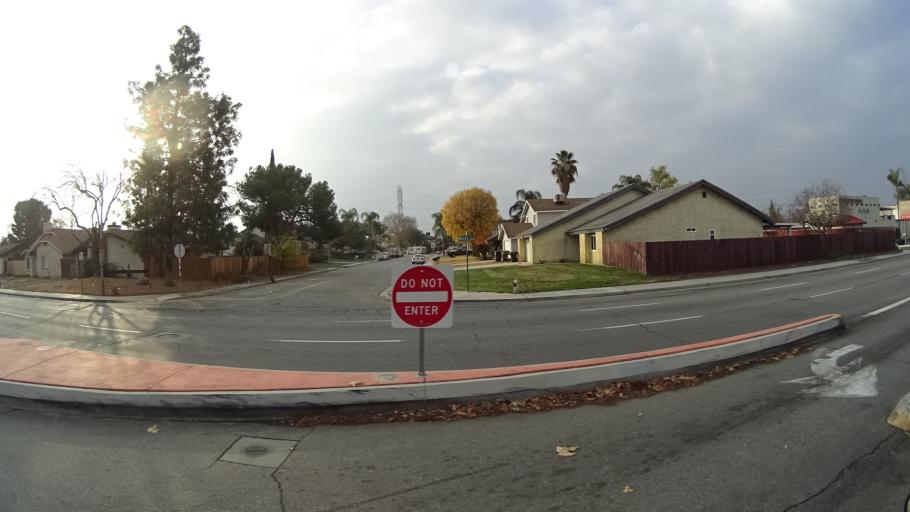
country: US
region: California
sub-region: Kern County
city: Bakersfield
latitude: 35.3177
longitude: -119.0518
